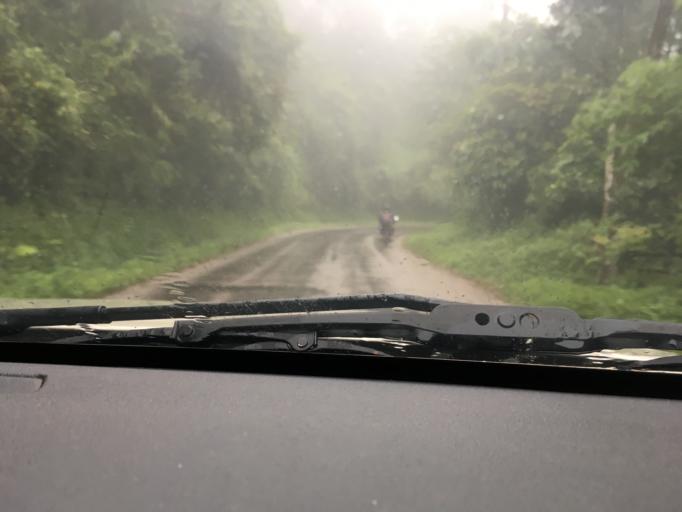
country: LA
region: Phongsali
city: Phongsali
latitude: 21.6623
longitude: 102.0882
